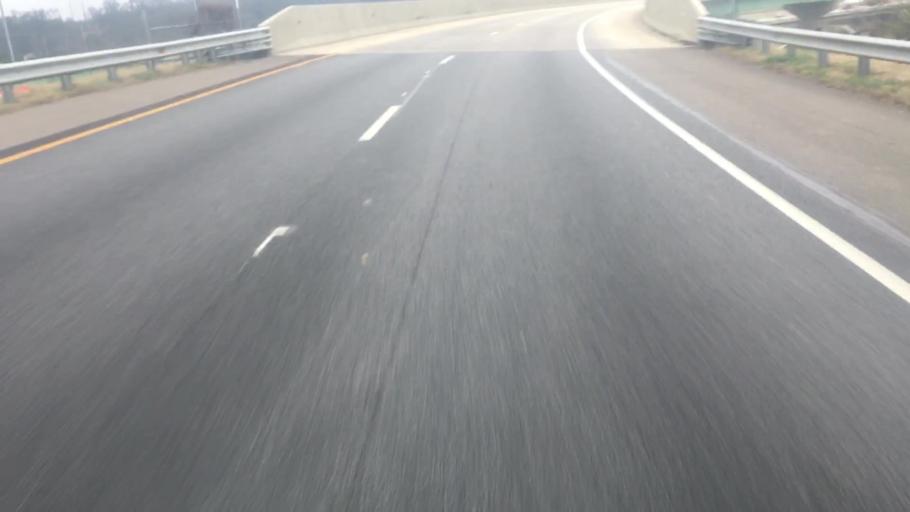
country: US
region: Alabama
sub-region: Jefferson County
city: Fultondale
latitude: 33.5742
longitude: -86.8196
